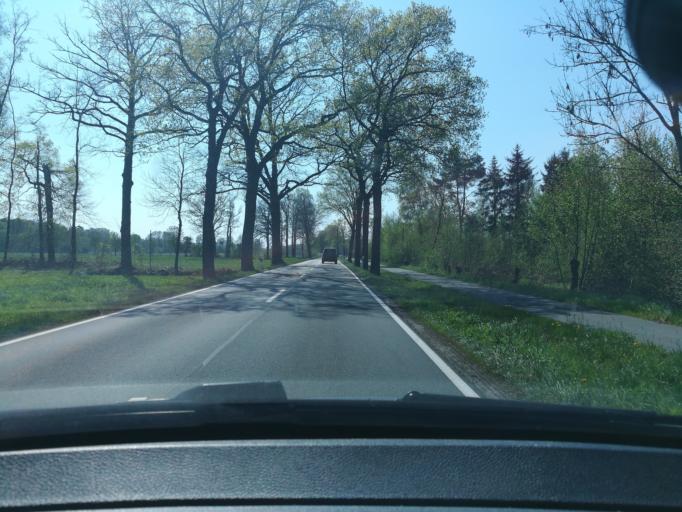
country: DE
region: North Rhine-Westphalia
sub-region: Regierungsbezirk Detmold
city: Harsewinkel
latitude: 52.0273
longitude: 8.2548
